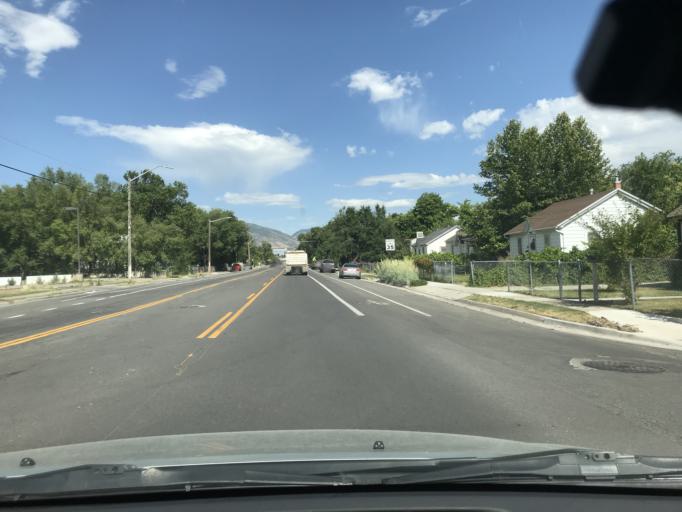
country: US
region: Utah
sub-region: Salt Lake County
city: Salt Lake City
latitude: 40.7606
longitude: -111.9270
